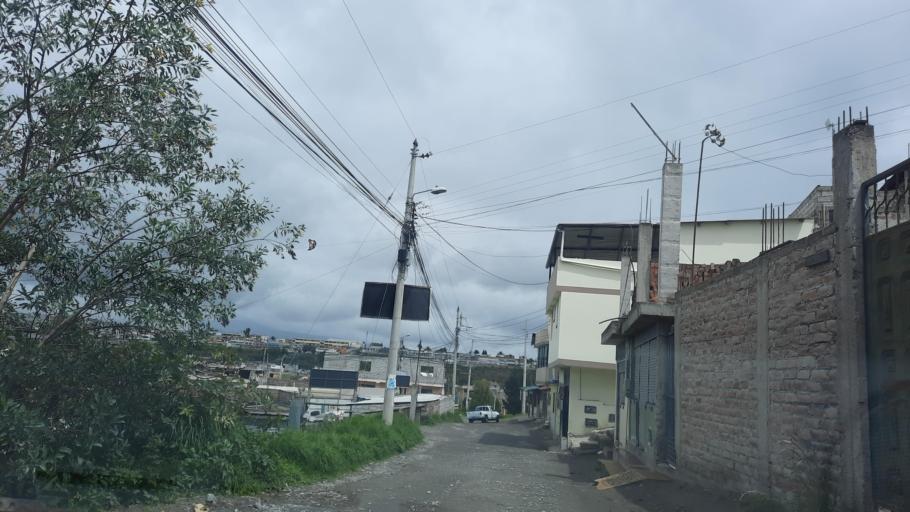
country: EC
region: Chimborazo
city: Riobamba
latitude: -1.6845
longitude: -78.6625
